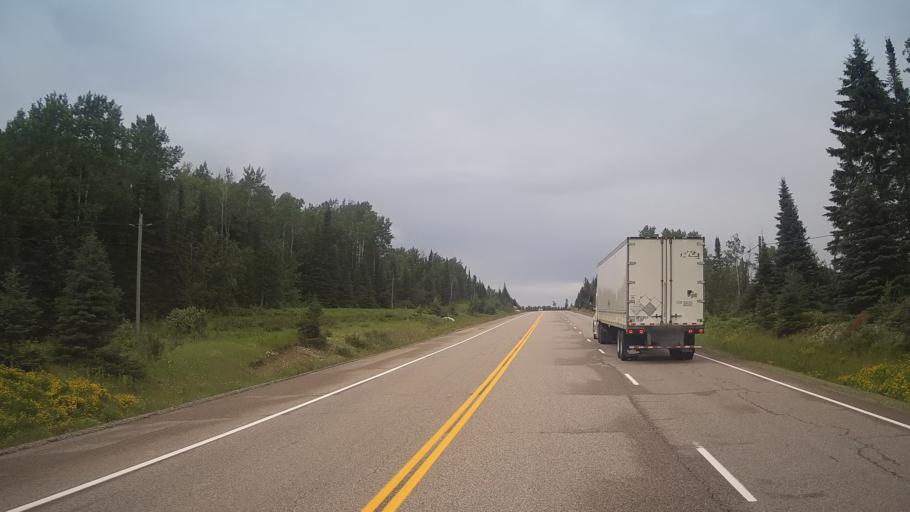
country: CA
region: Ontario
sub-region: Thunder Bay District
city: Thunder Bay
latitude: 48.7613
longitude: -89.8781
